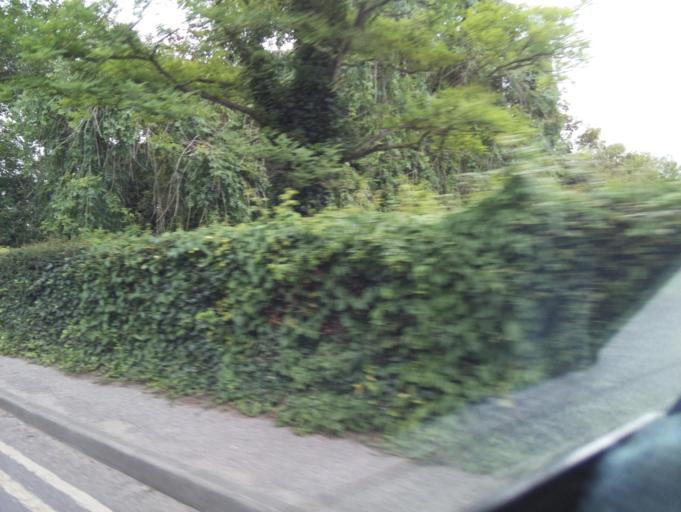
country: GB
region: England
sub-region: Hampshire
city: Eastleigh
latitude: 50.9702
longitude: -1.3436
